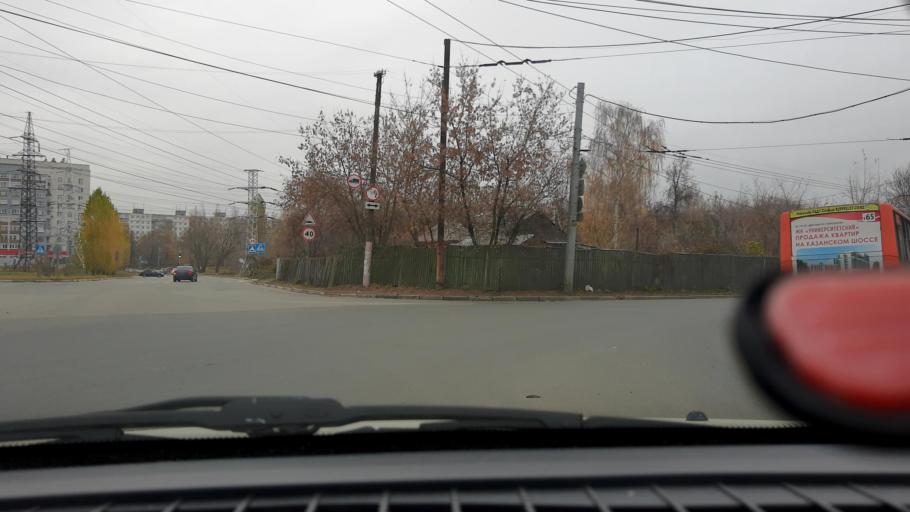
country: RU
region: Nizjnij Novgorod
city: Gorbatovka
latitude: 56.3331
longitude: 43.8604
